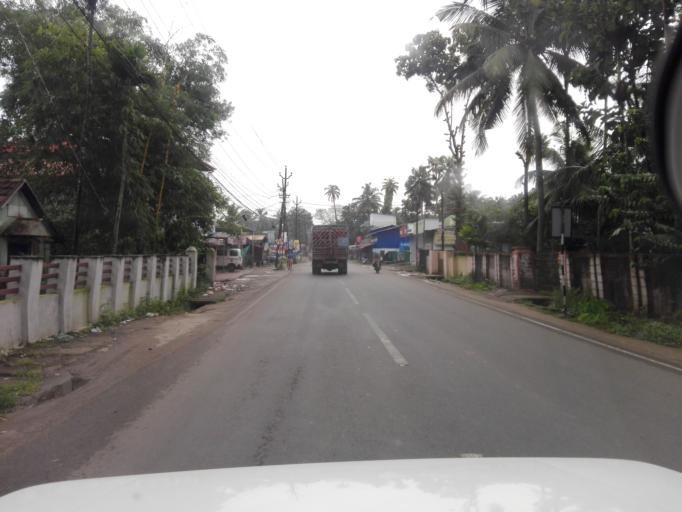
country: IN
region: Kerala
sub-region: Kottayam
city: Vaikam
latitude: 9.7577
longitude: 76.3977
